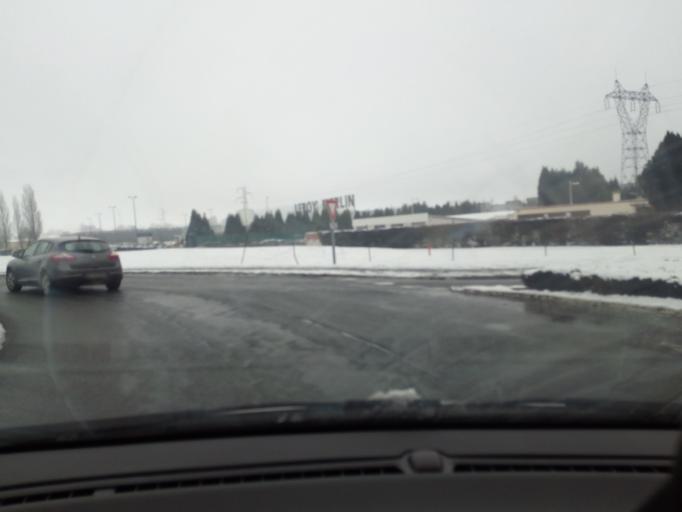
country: FR
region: Nord-Pas-de-Calais
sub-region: Departement du Nord
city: Hautmont
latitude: 50.2567
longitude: 3.9336
